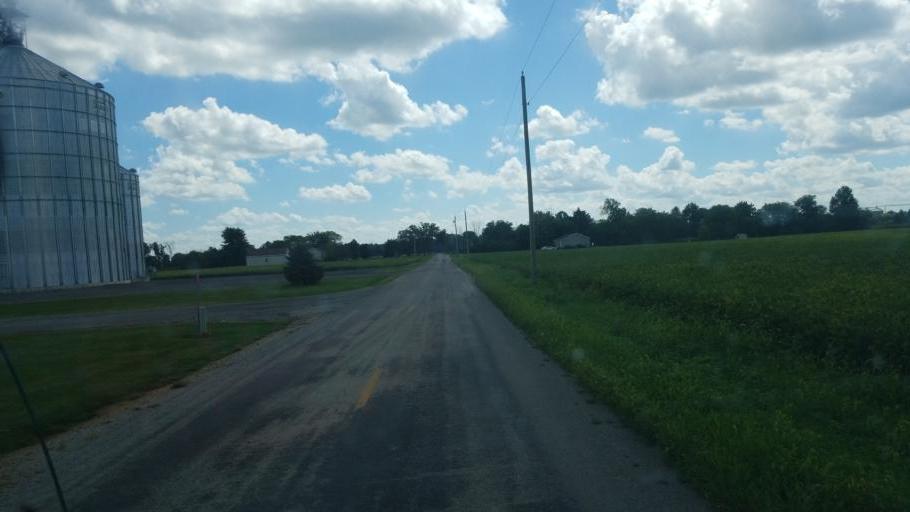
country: US
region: Ohio
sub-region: Marion County
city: Prospect
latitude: 40.4600
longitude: -83.1686
